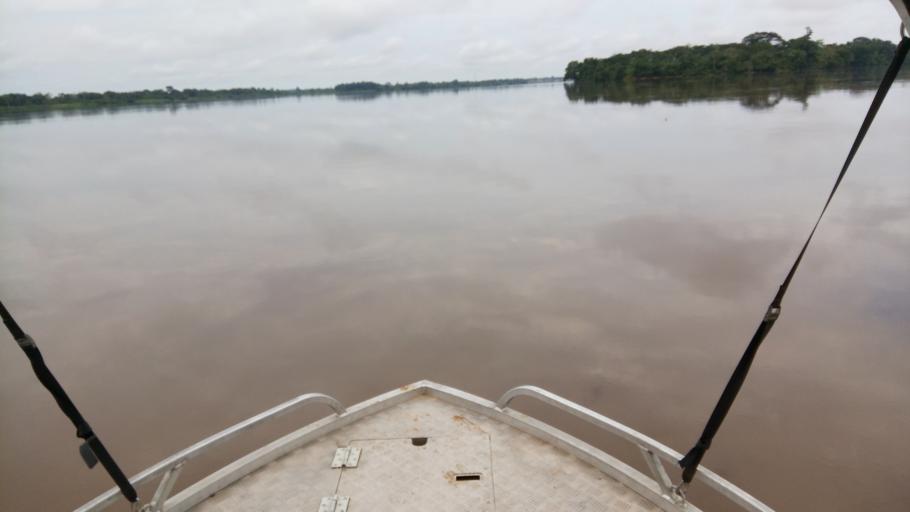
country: CD
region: Eastern Province
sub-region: Sous-Region de la Tshopo
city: Yangambi
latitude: 0.7671
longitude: 24.2989
